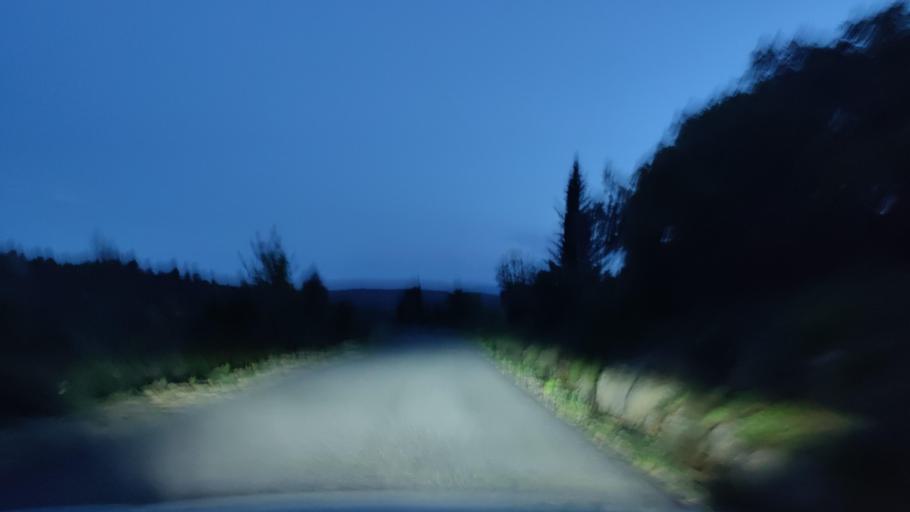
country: FR
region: Languedoc-Roussillon
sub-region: Departement des Pyrenees-Orientales
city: Estagel
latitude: 42.8789
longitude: 2.7443
